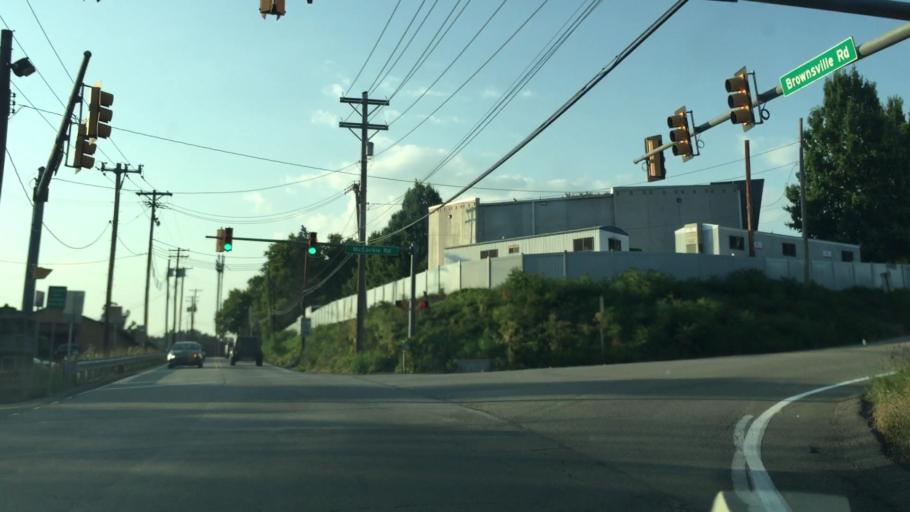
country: US
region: Pennsylvania
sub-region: Allegheny County
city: South Park Township
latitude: 40.3023
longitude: -79.9953
